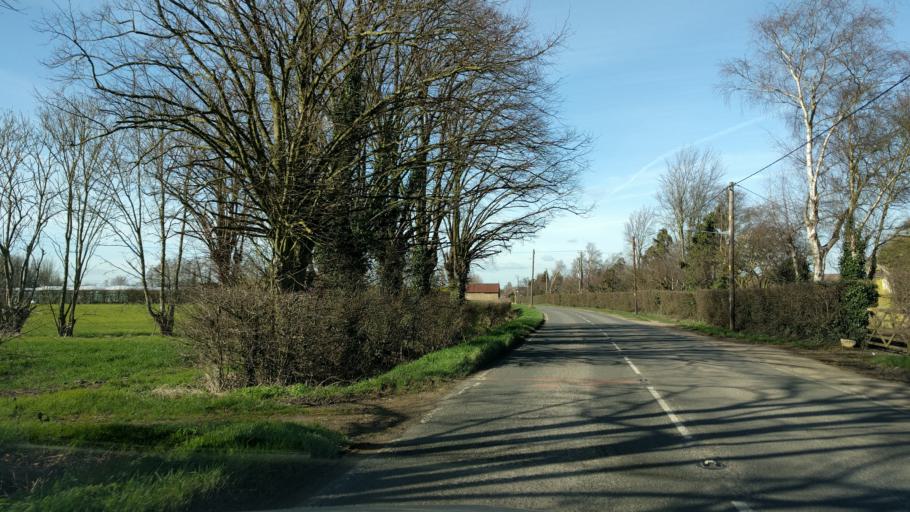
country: GB
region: England
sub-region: Cambridgeshire
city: Somersham
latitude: 52.3769
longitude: 0.0087
